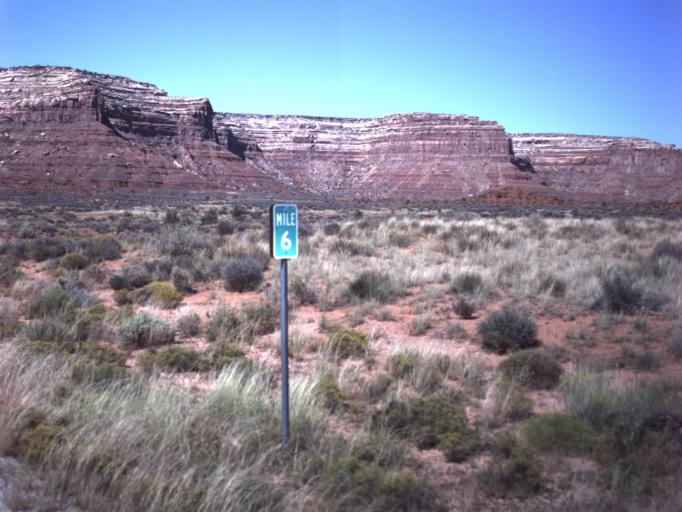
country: US
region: Utah
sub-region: San Juan County
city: Blanding
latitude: 37.2593
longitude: -109.9271
